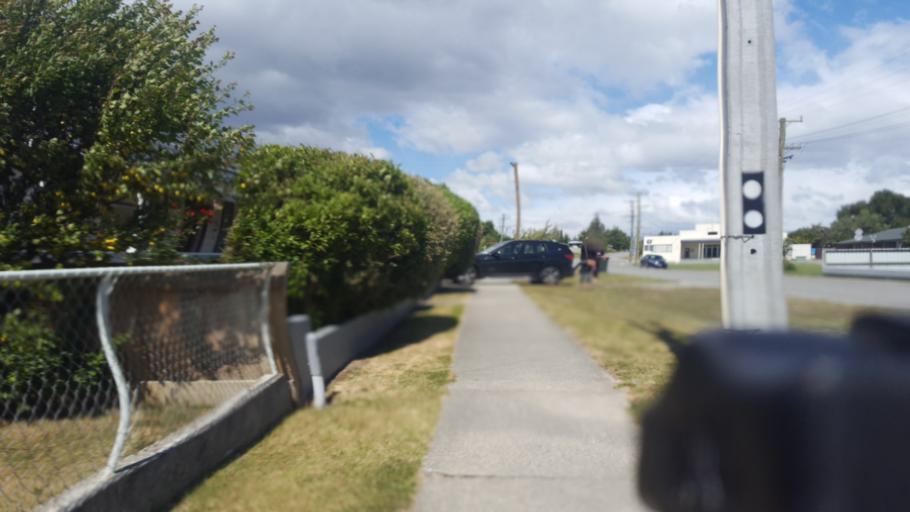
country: NZ
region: Otago
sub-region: Queenstown-Lakes District
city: Wanaka
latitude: -45.1874
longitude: 169.3191
